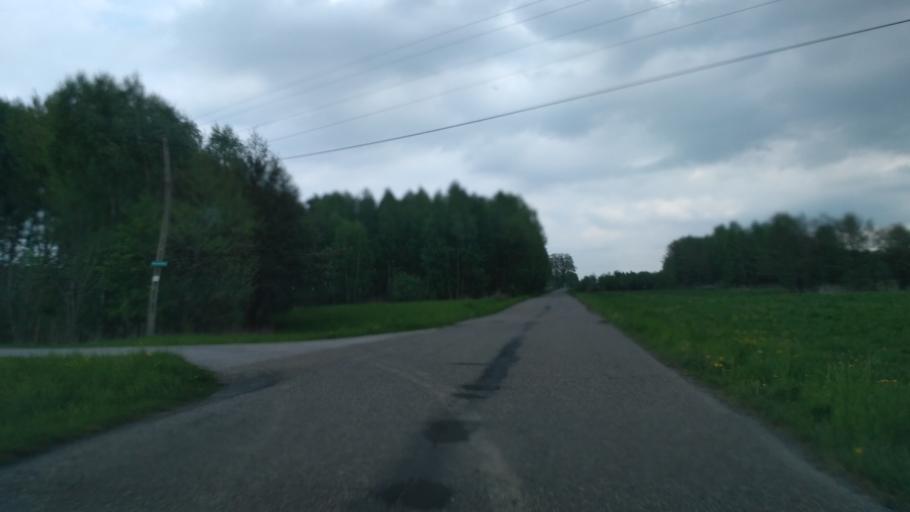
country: PL
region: Lesser Poland Voivodeship
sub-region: Powiat tarnowski
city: Szynwald
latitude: 49.9830
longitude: 21.1450
